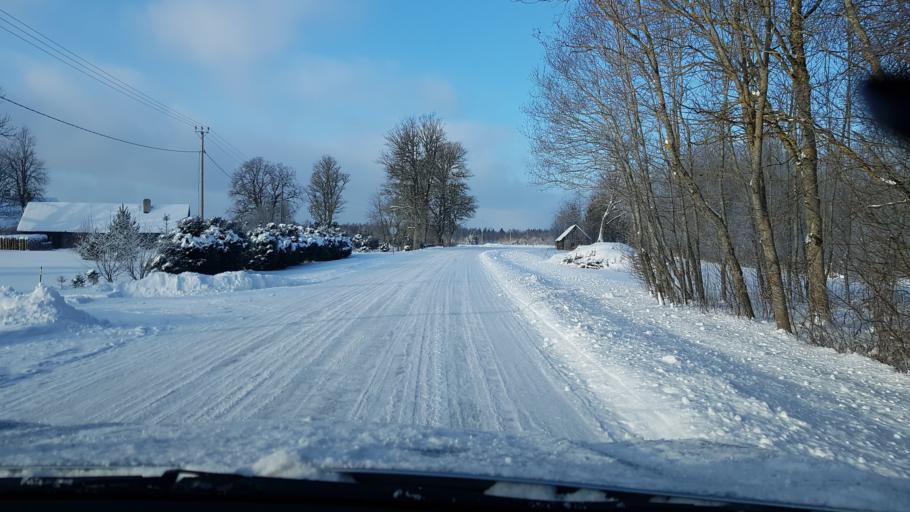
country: EE
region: Harju
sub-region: Nissi vald
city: Turba
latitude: 59.1076
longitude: 24.2303
